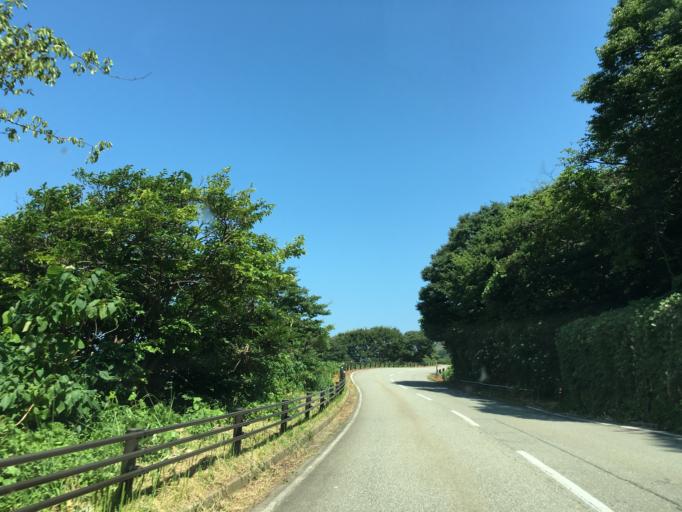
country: JP
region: Akita
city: Tenno
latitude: 39.8770
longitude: 139.7432
